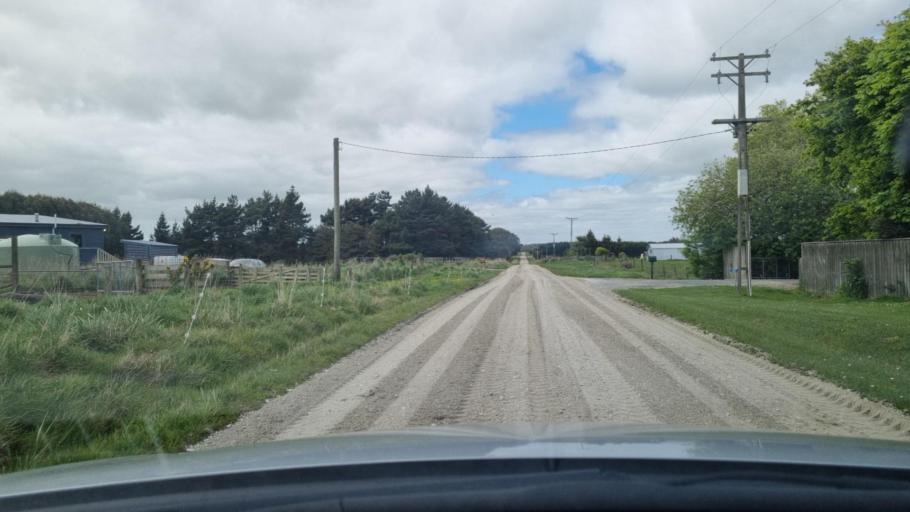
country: NZ
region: Southland
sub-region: Invercargill City
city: Invercargill
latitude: -46.4343
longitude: 168.4022
